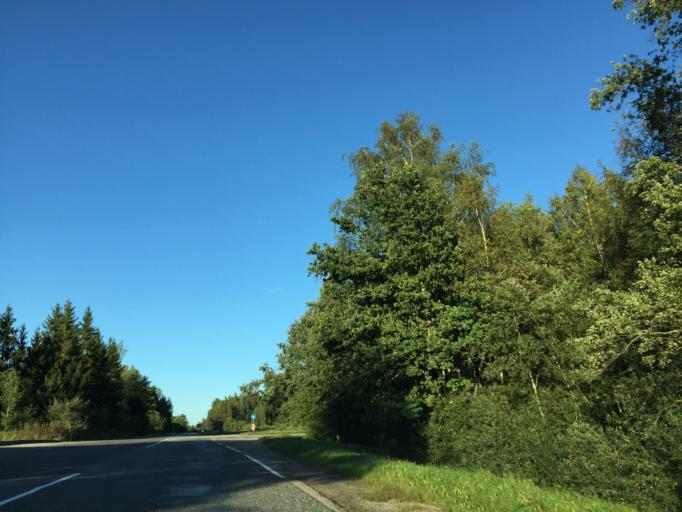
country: LV
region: Kuldigas Rajons
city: Kuldiga
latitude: 56.9794
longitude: 22.0147
